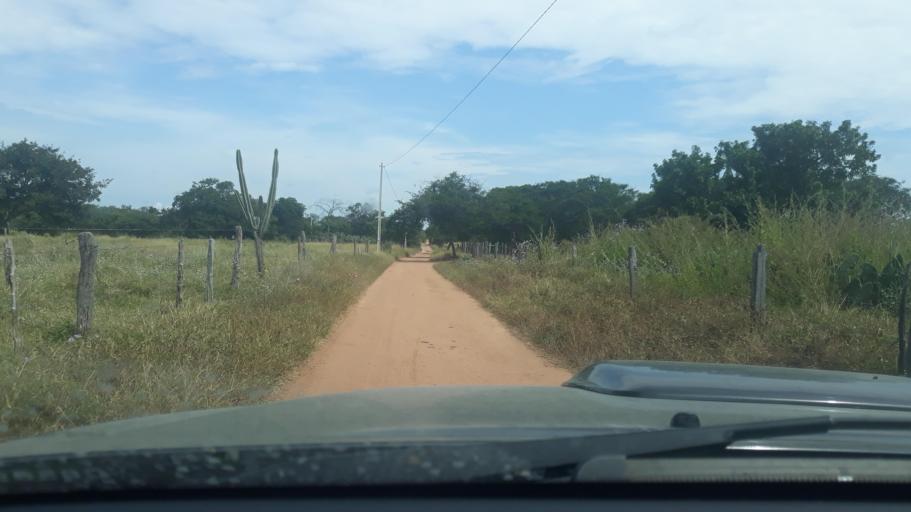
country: BR
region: Bahia
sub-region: Riacho De Santana
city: Riacho de Santana
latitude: -13.8607
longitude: -43.0320
